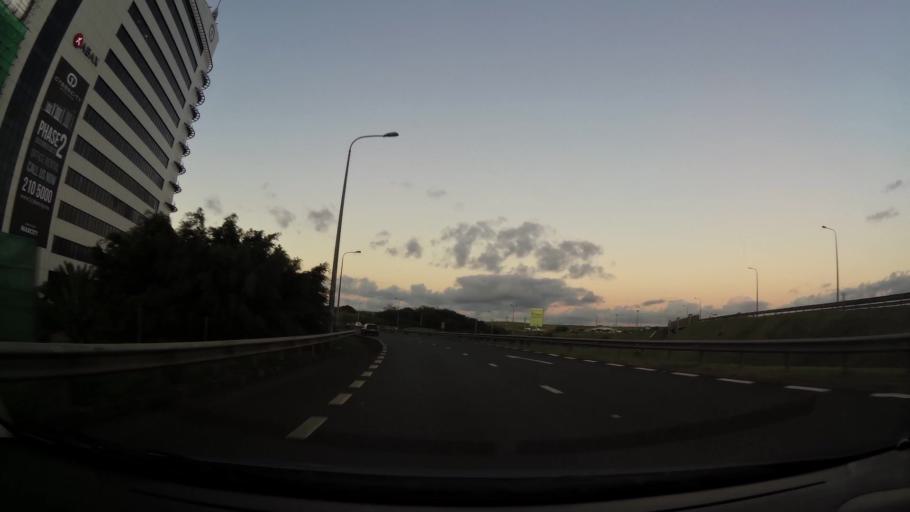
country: MU
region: Plaines Wilhems
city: Ebene
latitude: -20.2486
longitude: 57.4925
